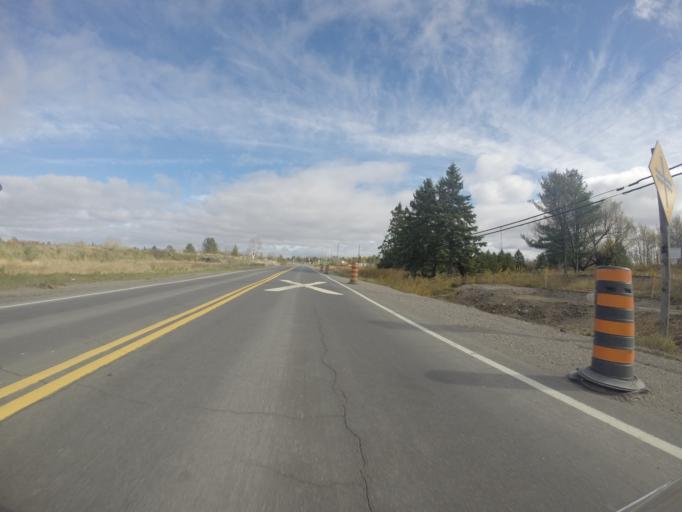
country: CA
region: Ontario
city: Greater Sudbury
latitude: 46.1046
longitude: -80.6631
